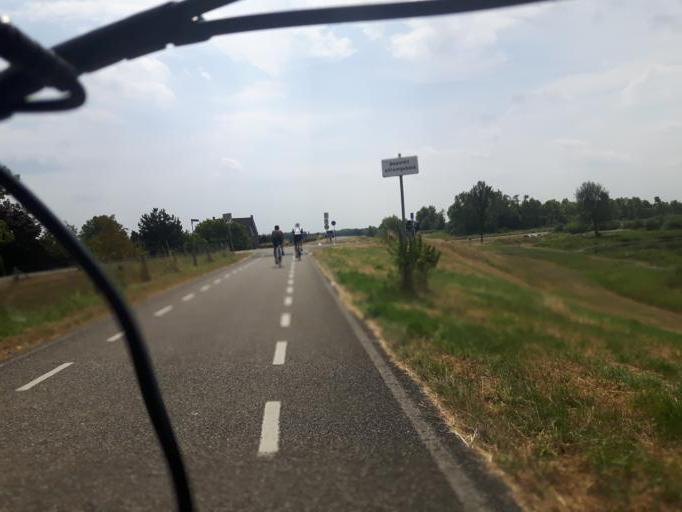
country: NL
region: Gelderland
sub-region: Gemeente Zaltbommel
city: Zaltbommel
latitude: 51.8186
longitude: 5.2057
